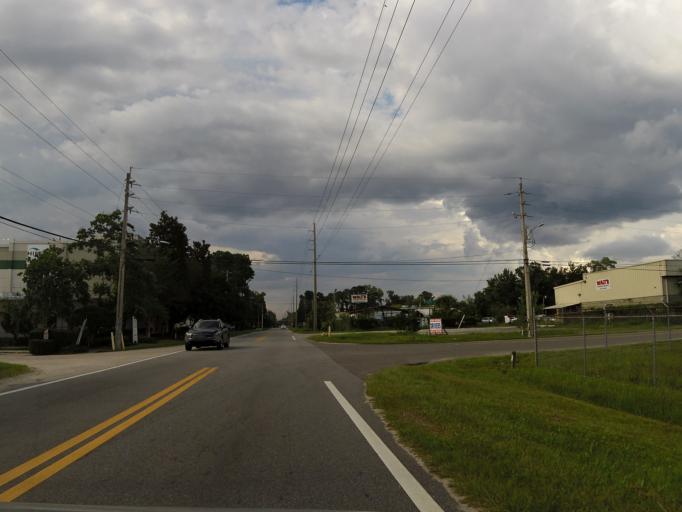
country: US
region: Florida
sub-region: Duval County
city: Jacksonville
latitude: 30.3319
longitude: -81.7435
